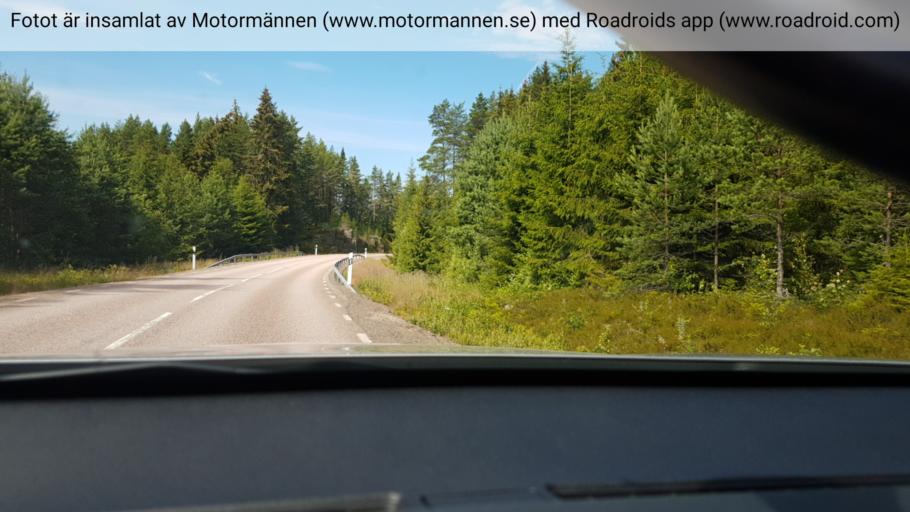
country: SE
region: Vaermland
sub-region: Munkfors Kommun
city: Munkfors
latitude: 59.8709
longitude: 13.3855
